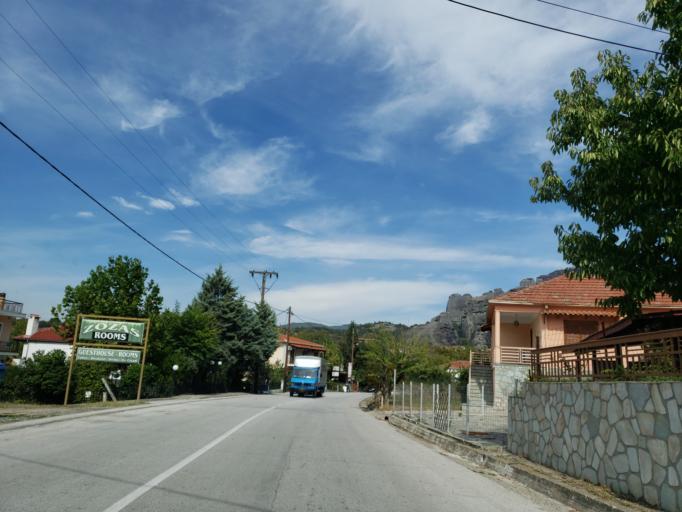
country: GR
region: Thessaly
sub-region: Trikala
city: Kastraki
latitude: 39.7133
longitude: 21.6160
